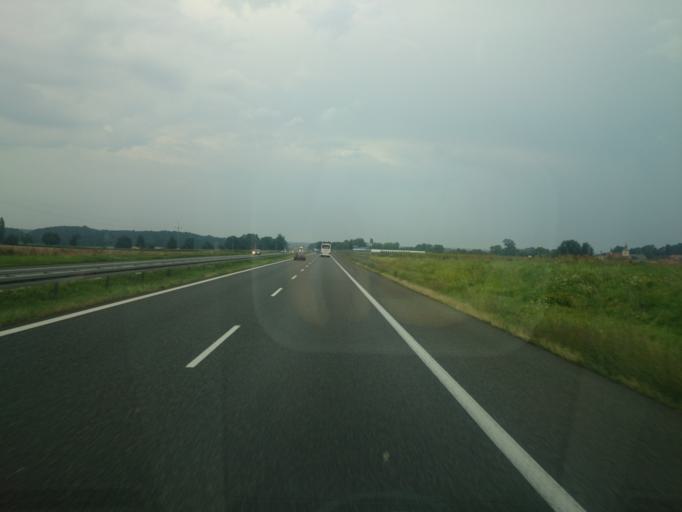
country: PL
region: Opole Voivodeship
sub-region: Powiat strzelecki
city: Ujazd
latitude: 50.4170
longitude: 18.4027
